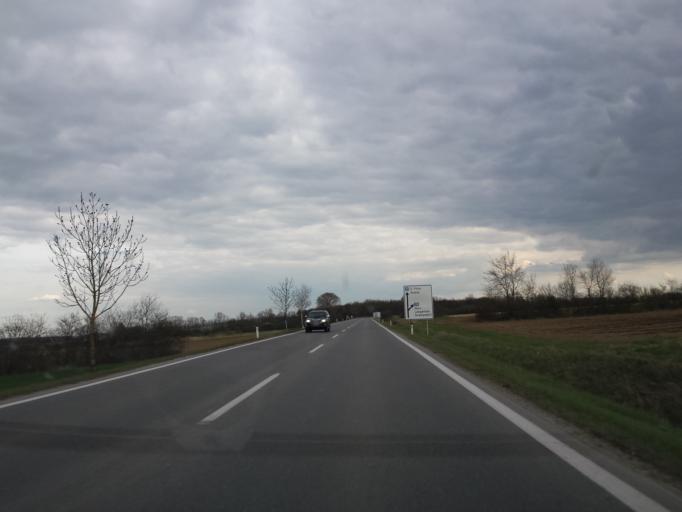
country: AT
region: Lower Austria
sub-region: Politischer Bezirk Krems
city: Stratzing
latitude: 48.4476
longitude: 15.6176
